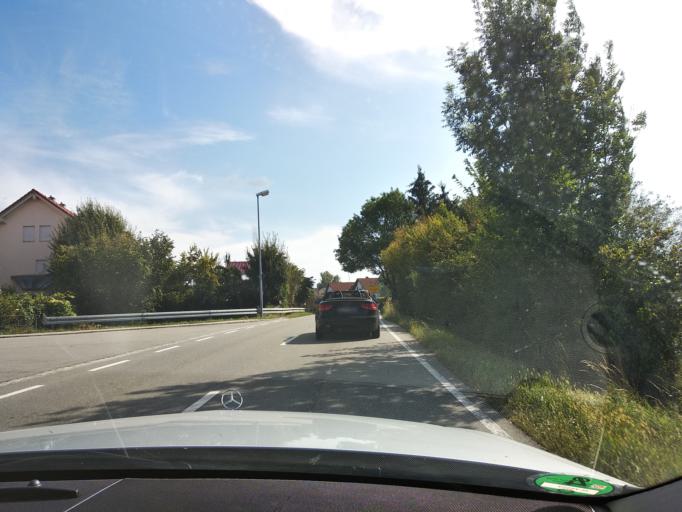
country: DE
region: Baden-Wuerttemberg
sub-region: Tuebingen Region
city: Amtzell
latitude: 47.6691
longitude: 9.7662
